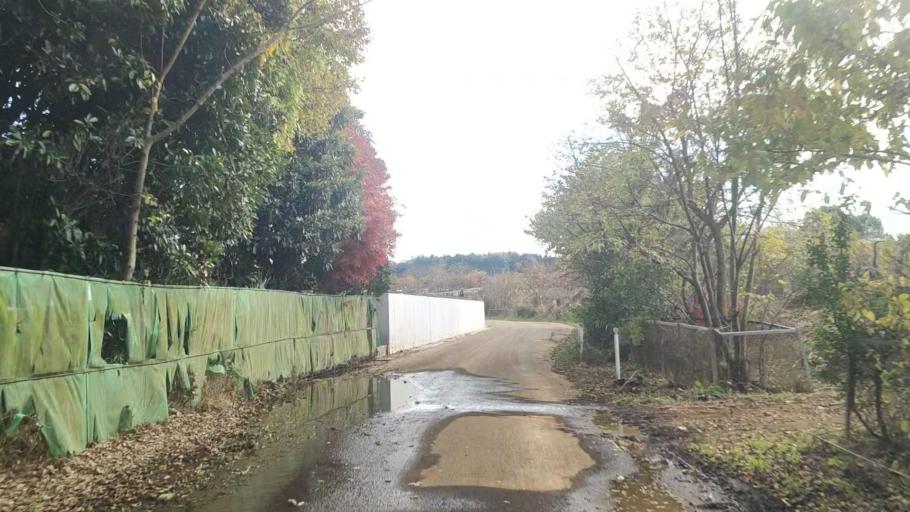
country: JP
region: Kanagawa
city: Minami-rinkan
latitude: 35.4882
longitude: 139.4932
